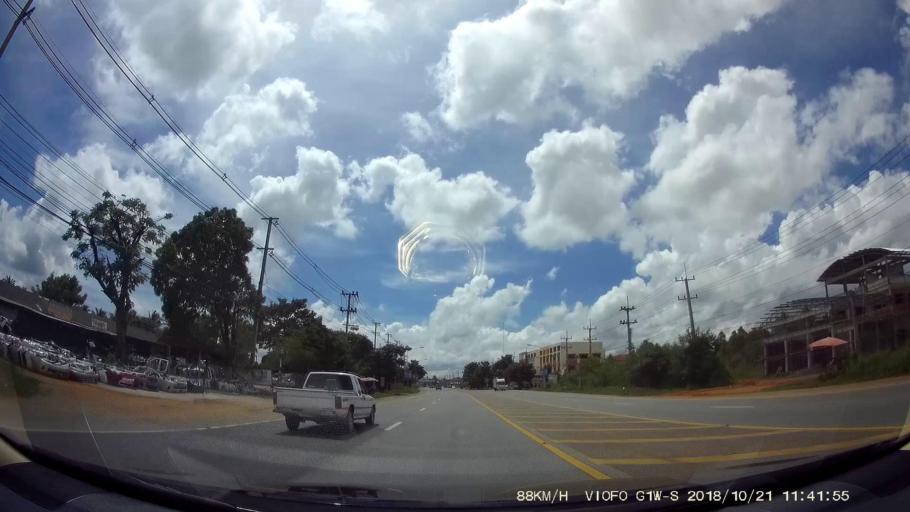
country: TH
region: Chaiyaphum
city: Chaiyaphum
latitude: 15.6926
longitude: 102.0122
